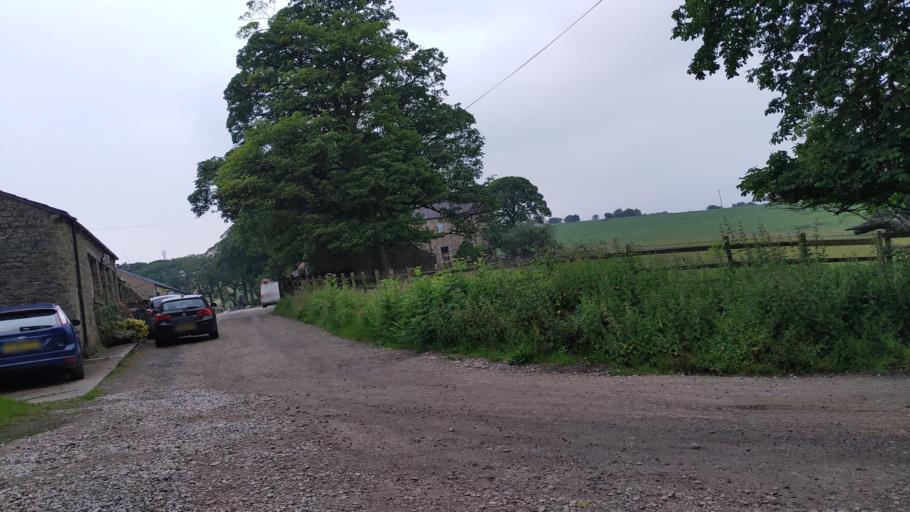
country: GB
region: England
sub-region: Lancashire
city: Chorley
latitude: 53.6842
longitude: -2.5722
